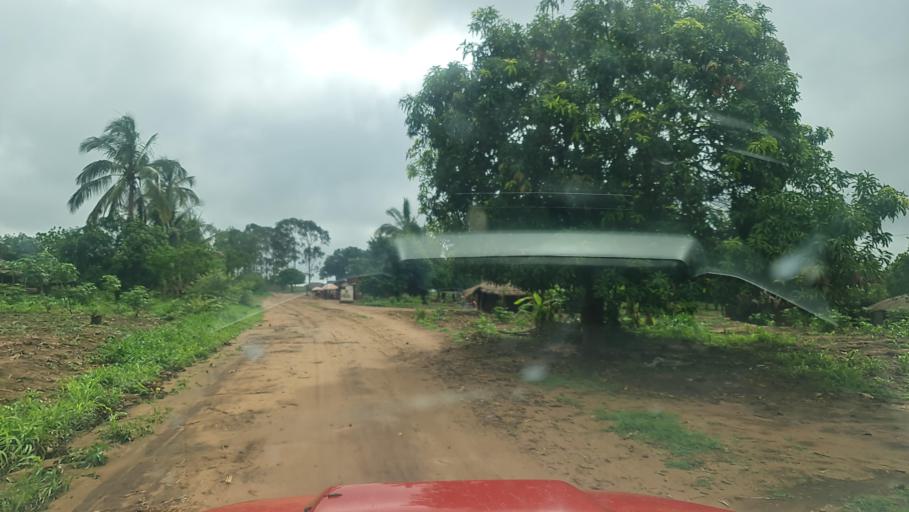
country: MW
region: Southern Region
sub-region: Nsanje District
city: Nsanje
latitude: -17.2033
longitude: 35.6960
